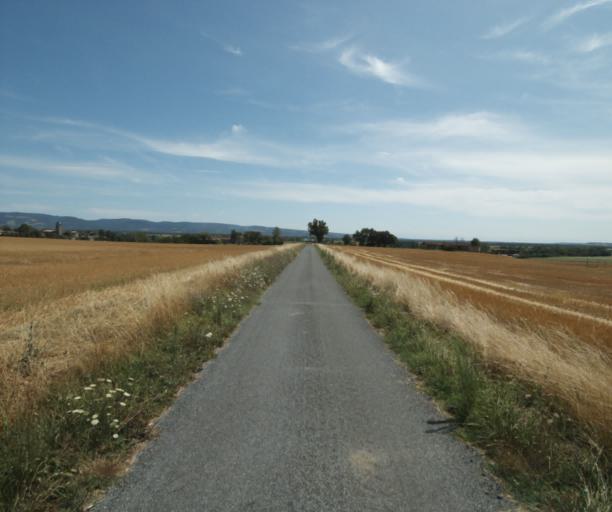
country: FR
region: Midi-Pyrenees
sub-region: Departement du Tarn
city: Puylaurens
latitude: 43.5321
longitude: 2.0031
